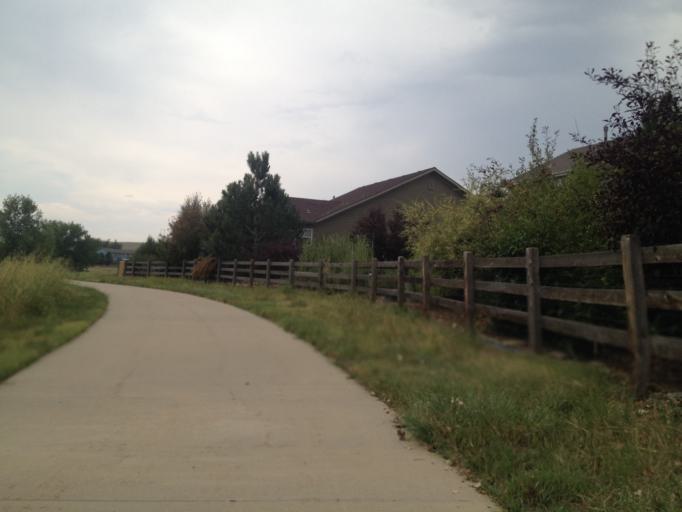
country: US
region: Colorado
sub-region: Boulder County
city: Erie
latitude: 40.0402
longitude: -105.0445
